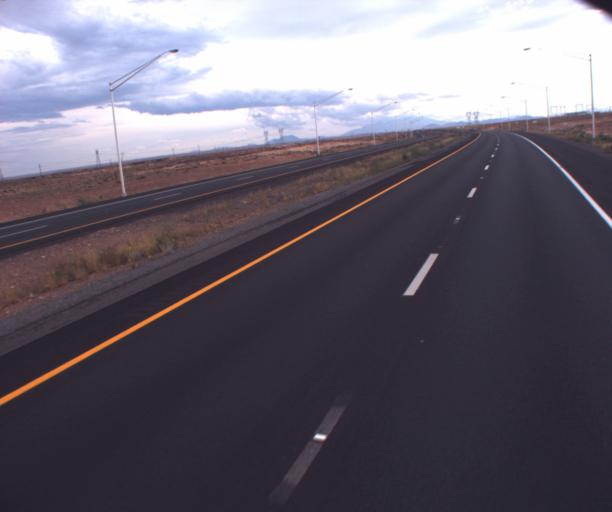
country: US
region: Arizona
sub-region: Coconino County
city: Tuba City
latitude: 35.8464
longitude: -111.4325
